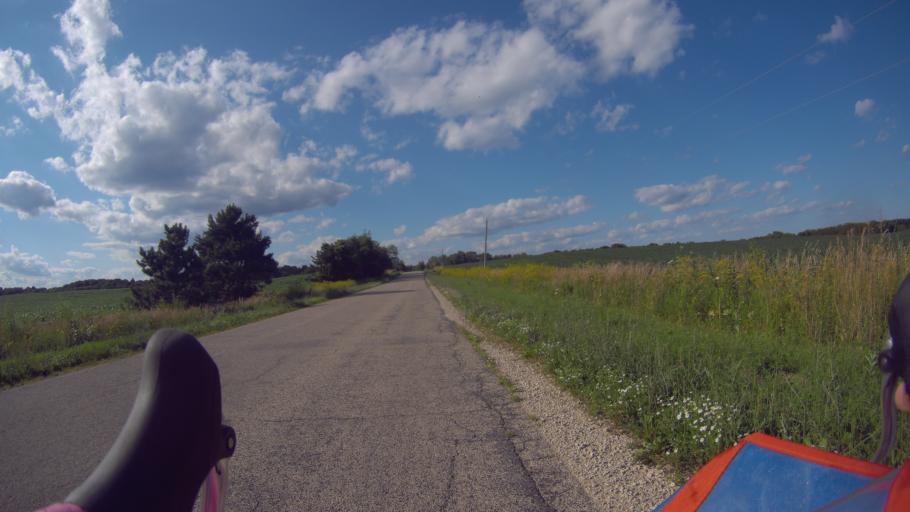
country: US
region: Wisconsin
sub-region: Dane County
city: Stoughton
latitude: 42.9341
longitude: -89.2940
